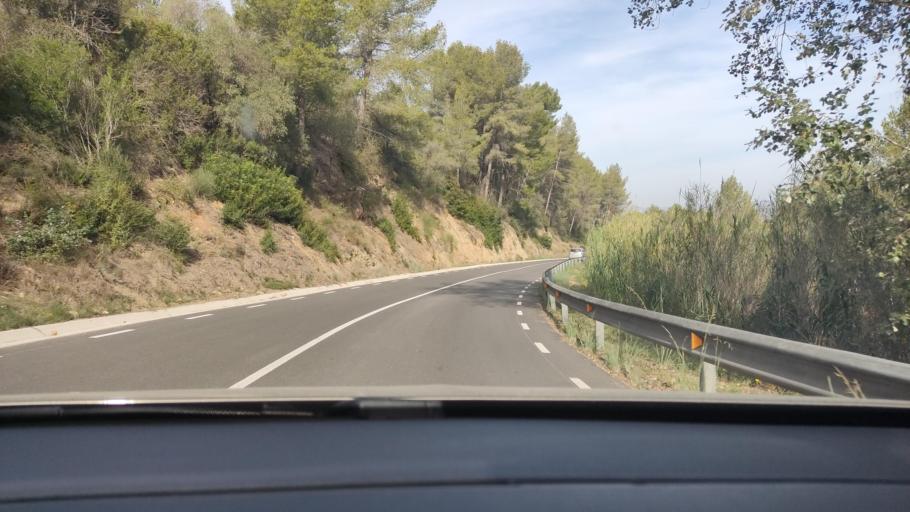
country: ES
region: Catalonia
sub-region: Provincia de Barcelona
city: Sant Sadurni d'Anoia
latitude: 41.4142
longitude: 1.8024
